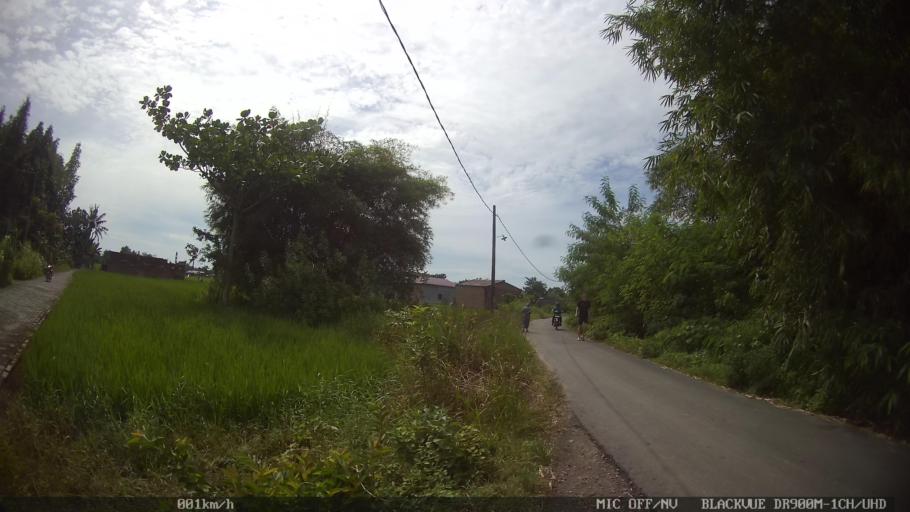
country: ID
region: North Sumatra
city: Percut
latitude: 3.6206
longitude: 98.7907
